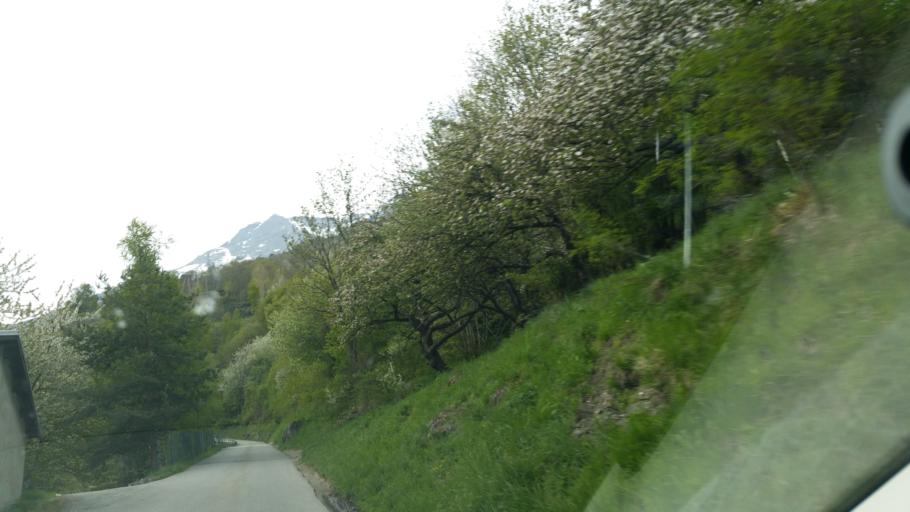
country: FR
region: Rhone-Alpes
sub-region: Departement de la Savoie
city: Modane
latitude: 45.2015
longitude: 6.6218
